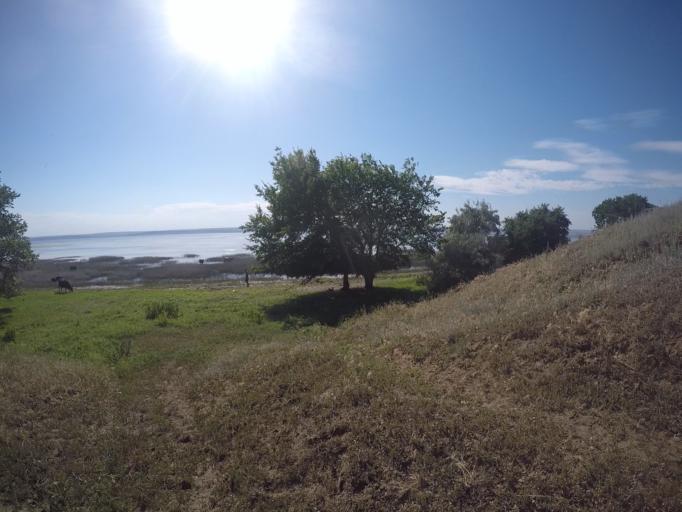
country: RU
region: Saratov
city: Privolzhskiy
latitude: 51.1963
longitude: 45.9097
